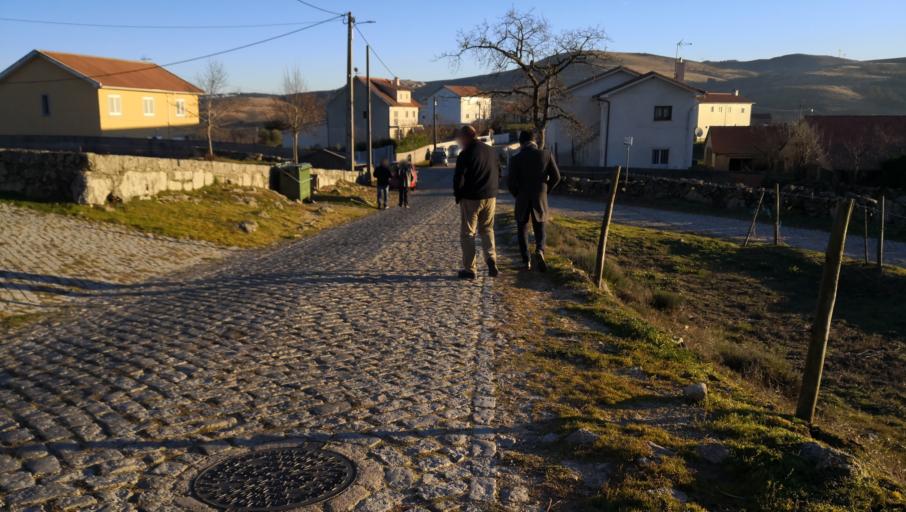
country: PT
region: Vila Real
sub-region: Ribeira de Pena
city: Ribeira de Pena
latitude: 41.5020
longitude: -7.7430
